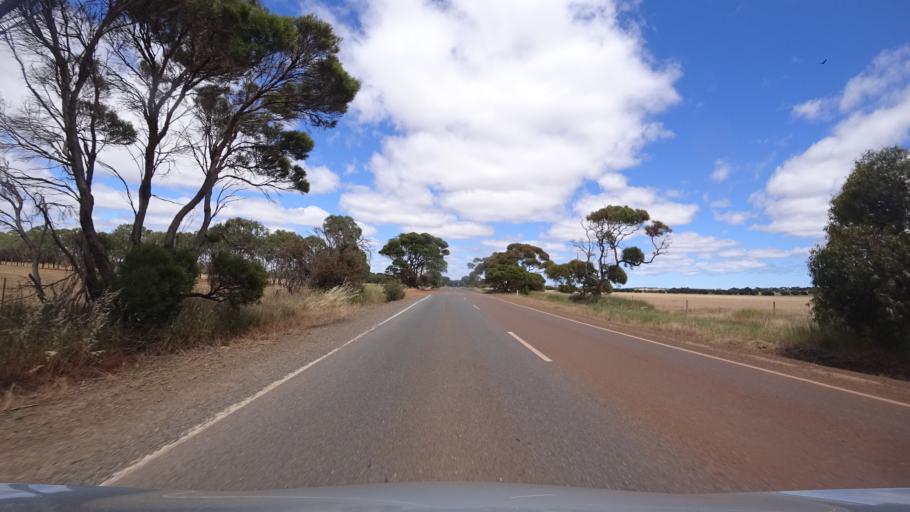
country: AU
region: South Australia
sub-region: Kangaroo Island
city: Kingscote
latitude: -35.6807
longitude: 137.5621
